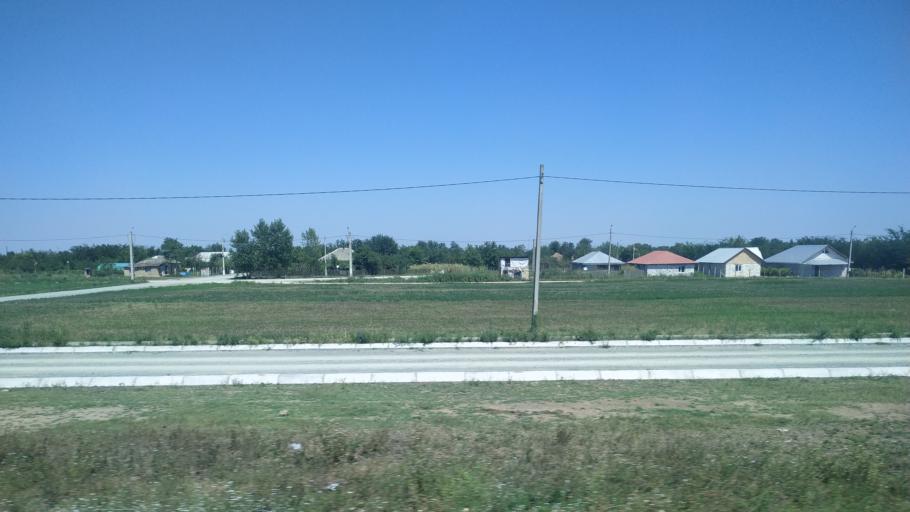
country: RO
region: Calarasi
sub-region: Comuna Perisoru
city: Perisoru
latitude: 44.4218
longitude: 27.6261
